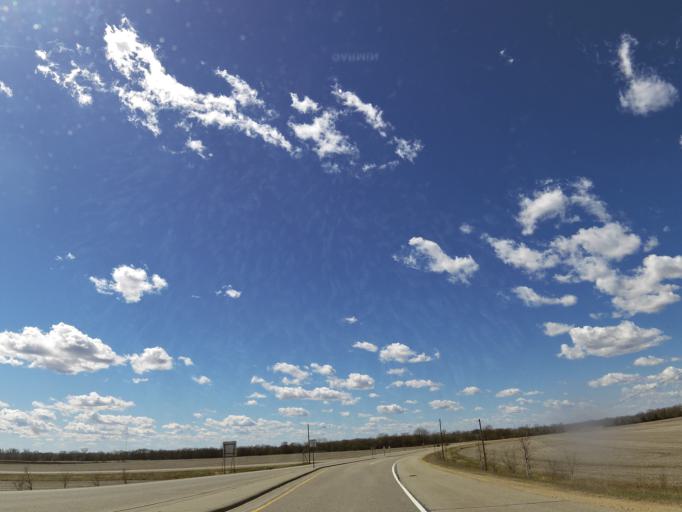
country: US
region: Minnesota
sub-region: Dakota County
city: Rosemount
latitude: 44.7104
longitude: -93.0355
